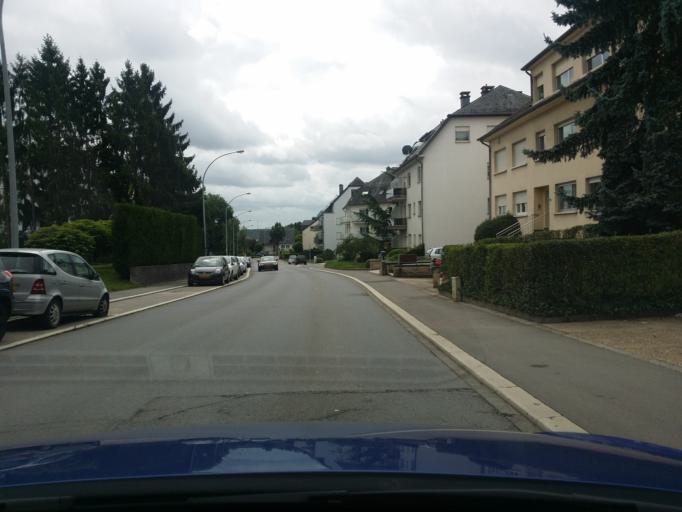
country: LU
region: Luxembourg
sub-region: Canton de Luxembourg
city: Strassen
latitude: 49.6207
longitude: 6.0646
